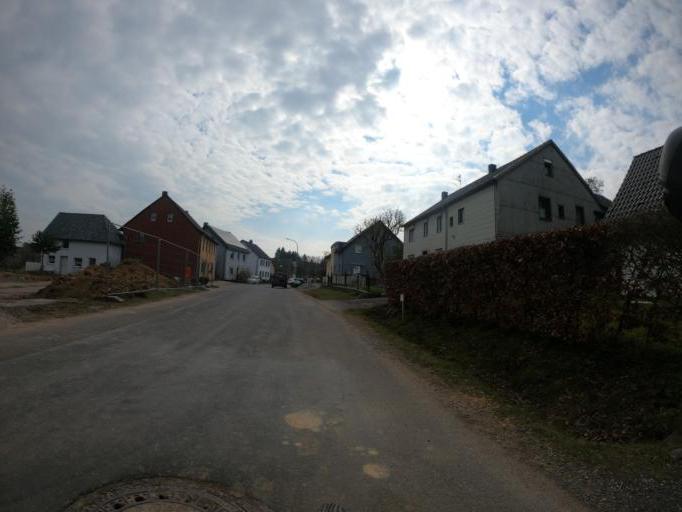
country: DE
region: North Rhine-Westphalia
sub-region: Regierungsbezirk Koln
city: Roetgen
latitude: 50.6518
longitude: 6.1991
